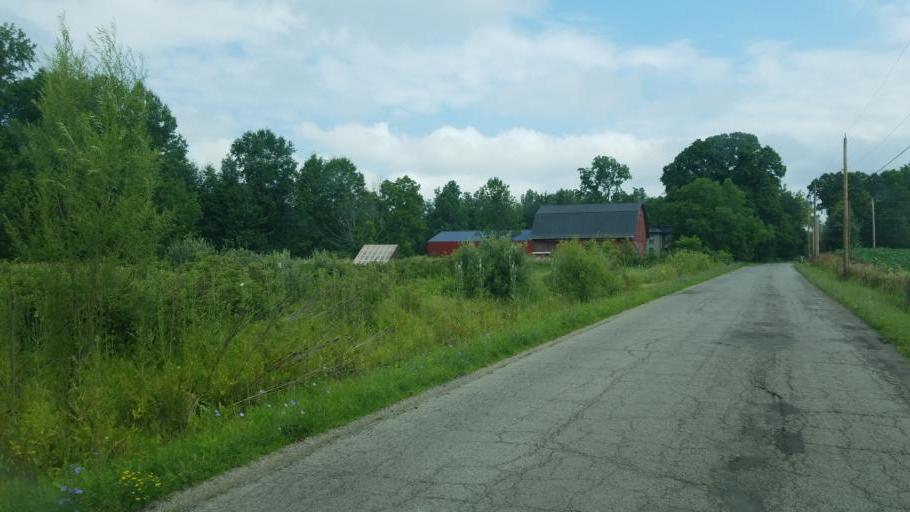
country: US
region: Ohio
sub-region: Crawford County
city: Galion
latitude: 40.7074
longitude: -82.7836
